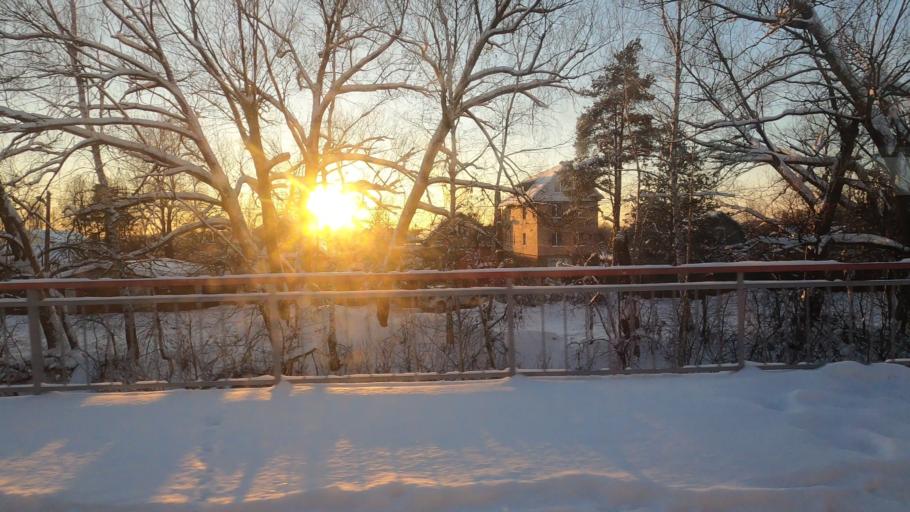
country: RU
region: Moskovskaya
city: Dmitrov
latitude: 56.3819
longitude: 37.5172
